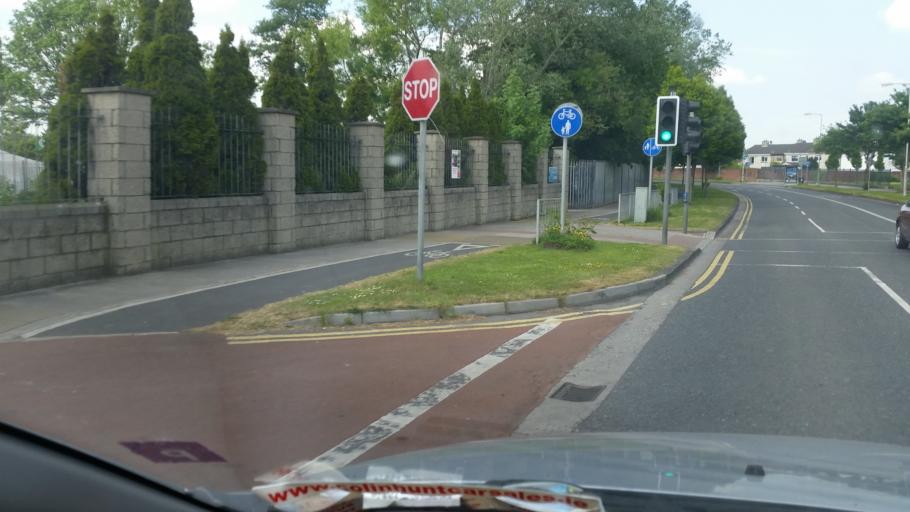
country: IE
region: Leinster
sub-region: Fingal County
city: Blanchardstown
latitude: 53.3969
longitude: -6.3996
